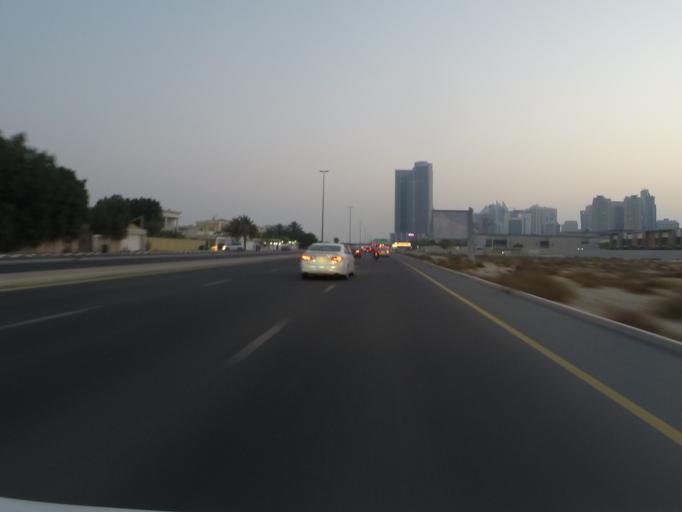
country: AE
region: Dubai
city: Dubai
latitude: 25.1023
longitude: 55.1863
